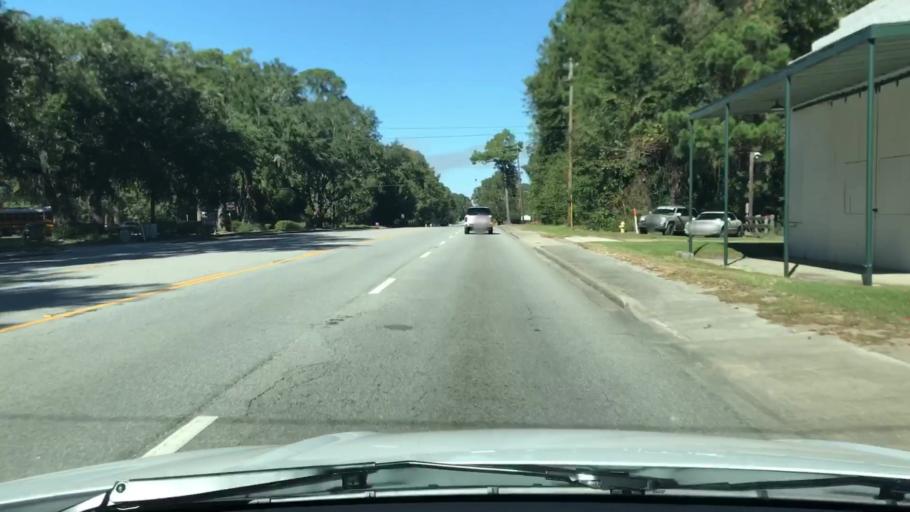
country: US
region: South Carolina
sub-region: Beaufort County
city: Laurel Bay
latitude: 32.5544
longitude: -80.7439
